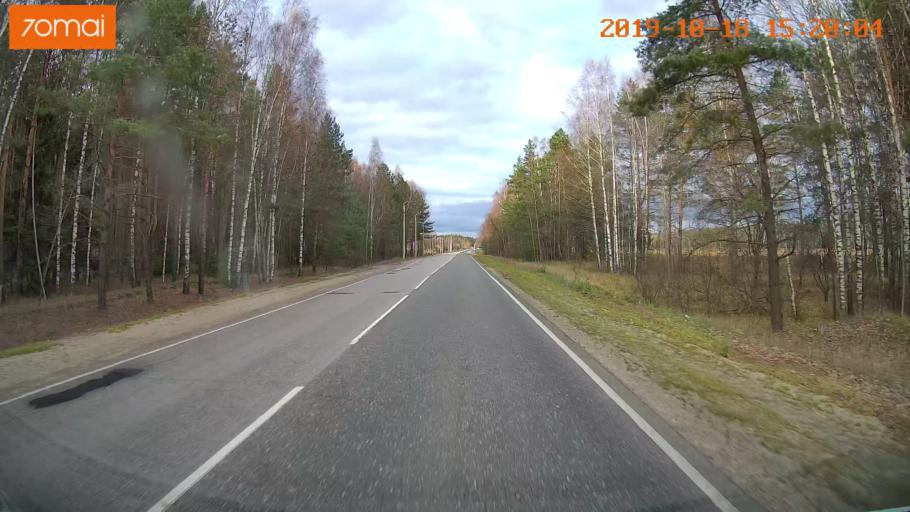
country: RU
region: Vladimir
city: Anopino
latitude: 55.6824
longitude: 40.7424
